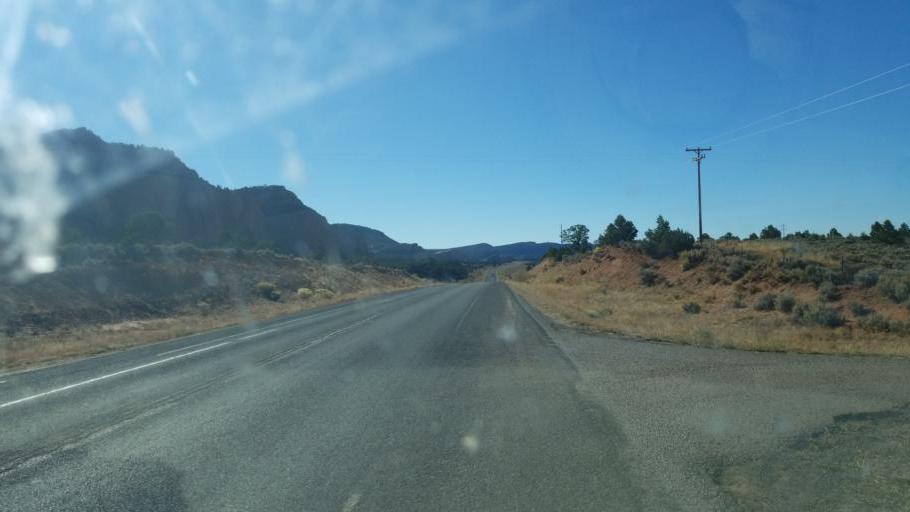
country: US
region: New Mexico
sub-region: McKinley County
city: Navajo
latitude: 35.8913
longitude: -109.0268
